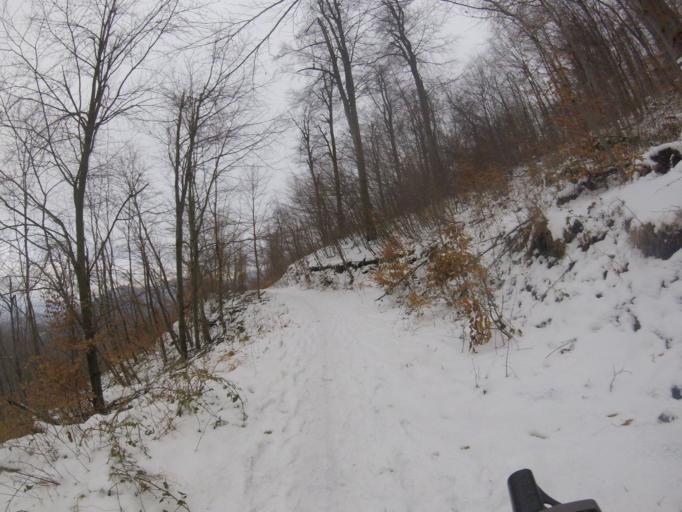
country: HU
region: Pest
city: Dunabogdany
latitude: 47.7532
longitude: 19.0120
